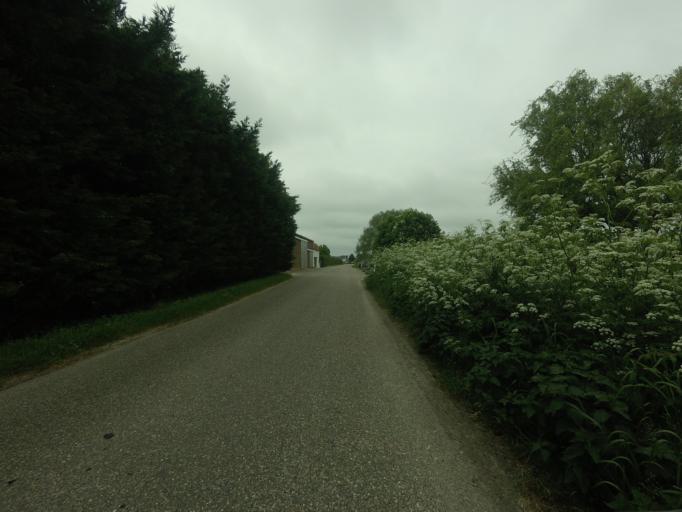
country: NL
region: South Holland
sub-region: Gemeente Goeree-Overflakkee
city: Middelharnis
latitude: 51.7200
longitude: 4.2086
